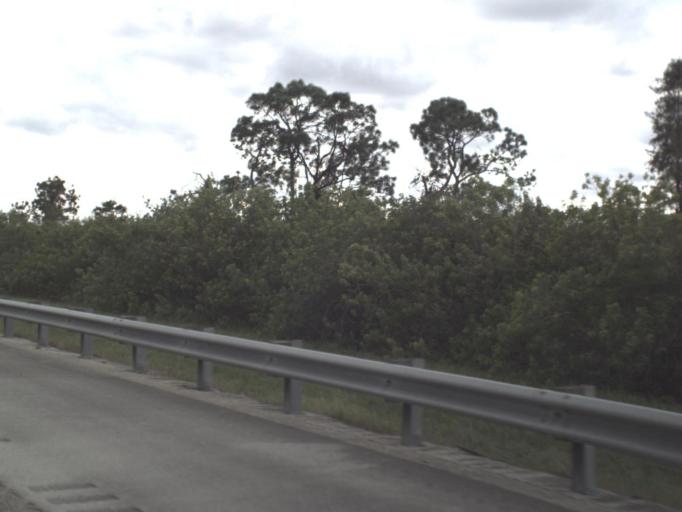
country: US
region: Florida
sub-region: Martin County
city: Hobe Sound
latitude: 27.0396
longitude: -80.2394
